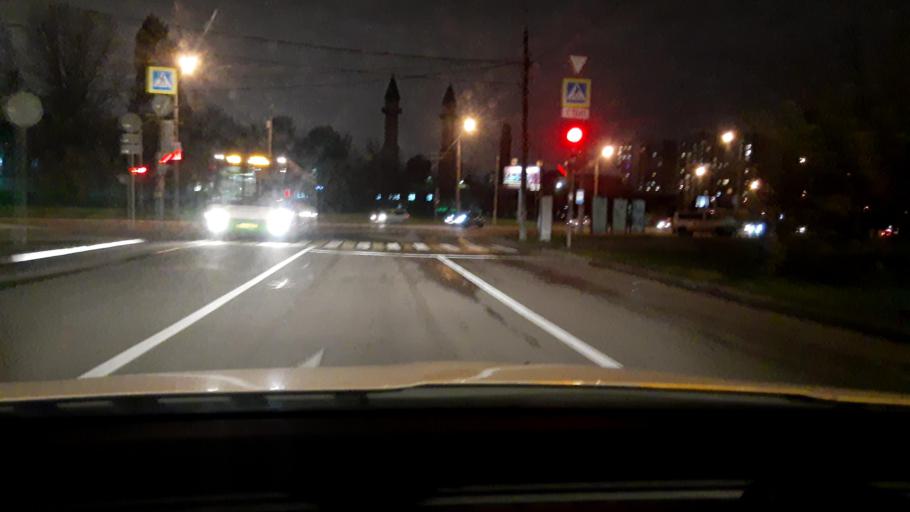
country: RU
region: Moscow
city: Otradnoye
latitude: 55.8583
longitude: 37.5947
